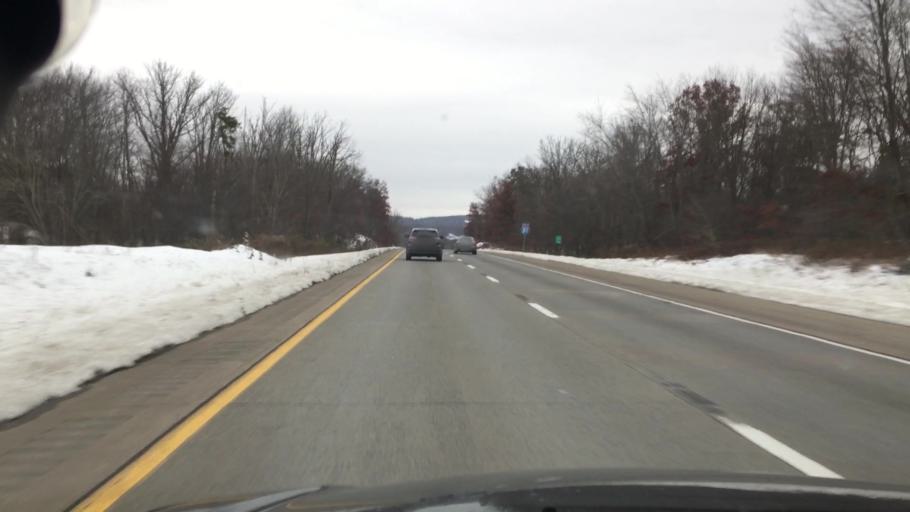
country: US
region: Pennsylvania
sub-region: Luzerne County
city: Nanticoke
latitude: 41.1207
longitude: -75.9622
